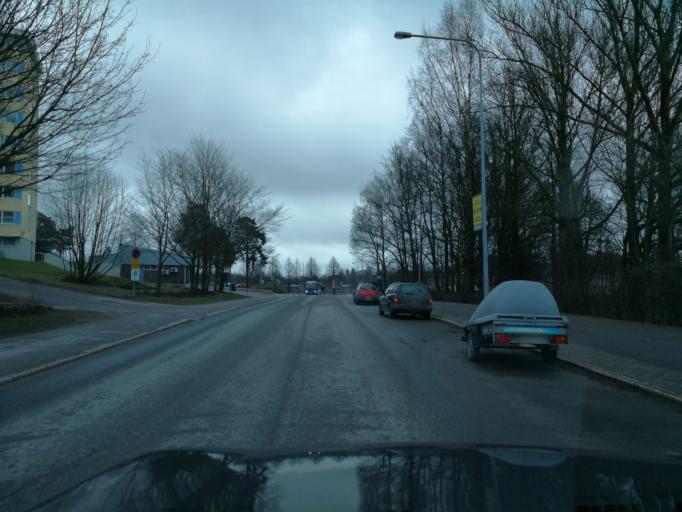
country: FI
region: Uusimaa
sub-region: Helsinki
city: Helsinki
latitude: 60.2168
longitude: 24.9656
